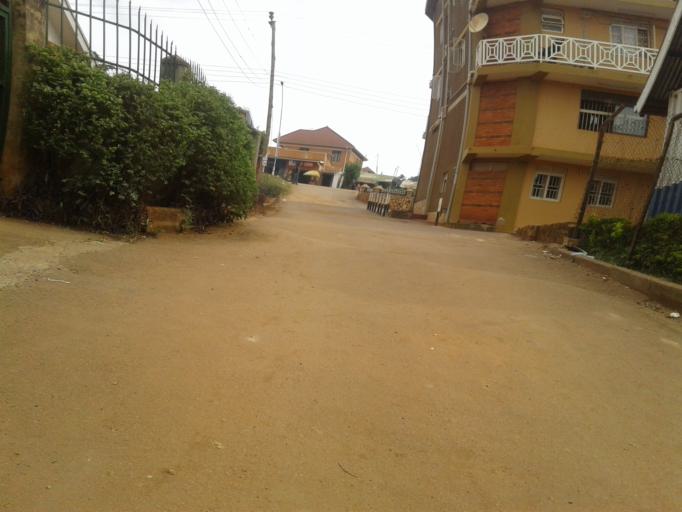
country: UG
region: Central Region
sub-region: Kampala District
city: Kampala
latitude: 0.2664
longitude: 32.6231
